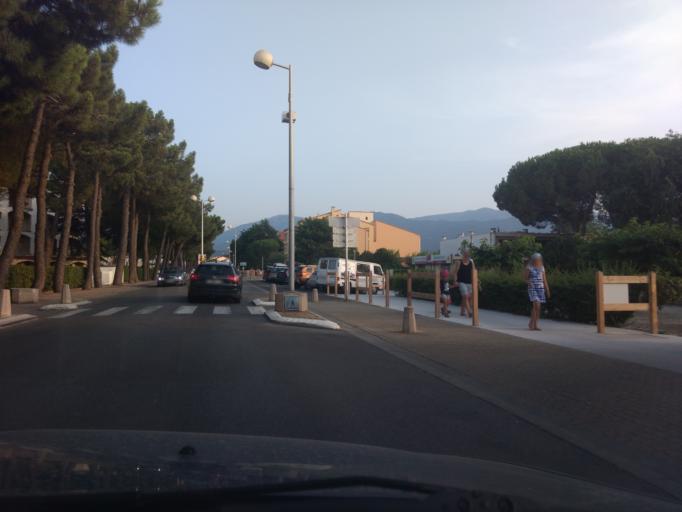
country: FR
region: Languedoc-Roussillon
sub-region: Departement des Pyrenees-Orientales
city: Argelers
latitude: 42.5609
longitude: 3.0411
